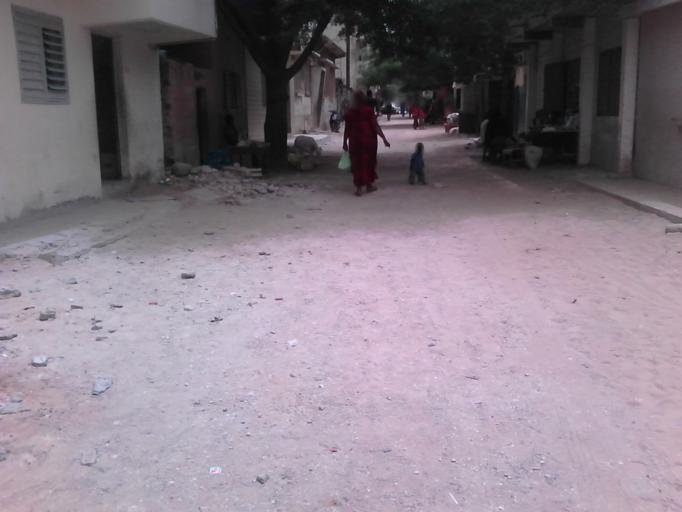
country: SN
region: Dakar
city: Grand Dakar
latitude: 14.7058
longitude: -17.4543
